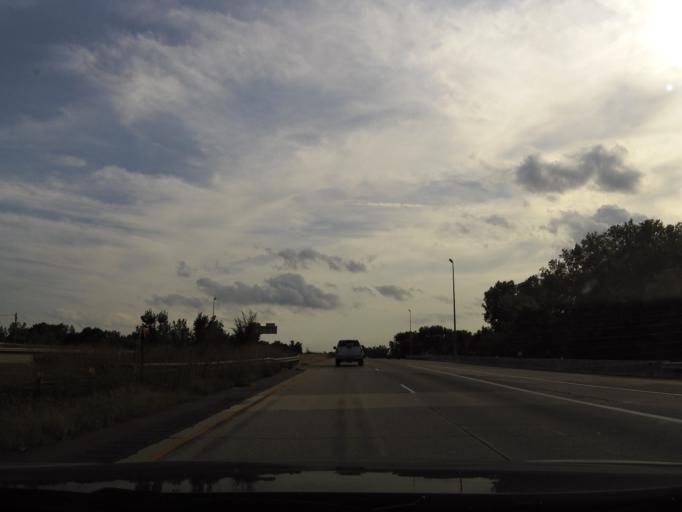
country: US
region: Minnesota
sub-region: Dakota County
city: Lakeville
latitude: 44.6954
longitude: -93.2896
